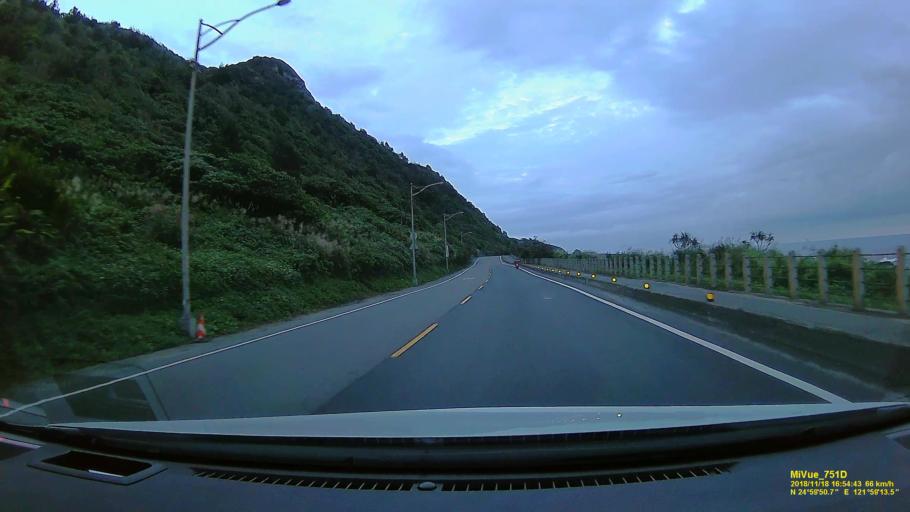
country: TW
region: Taiwan
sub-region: Keelung
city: Keelung
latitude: 24.9974
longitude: 121.9871
